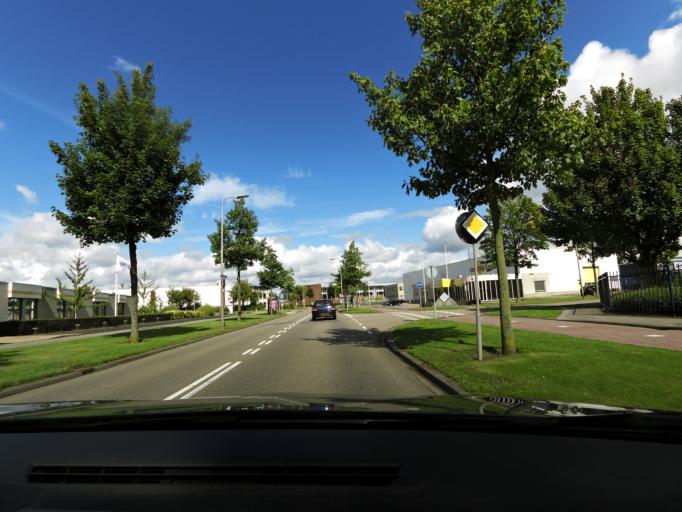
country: NL
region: South Holland
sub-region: Gemeente Oud-Beijerland
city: Oud-Beijerland
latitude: 51.8268
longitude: 4.4320
